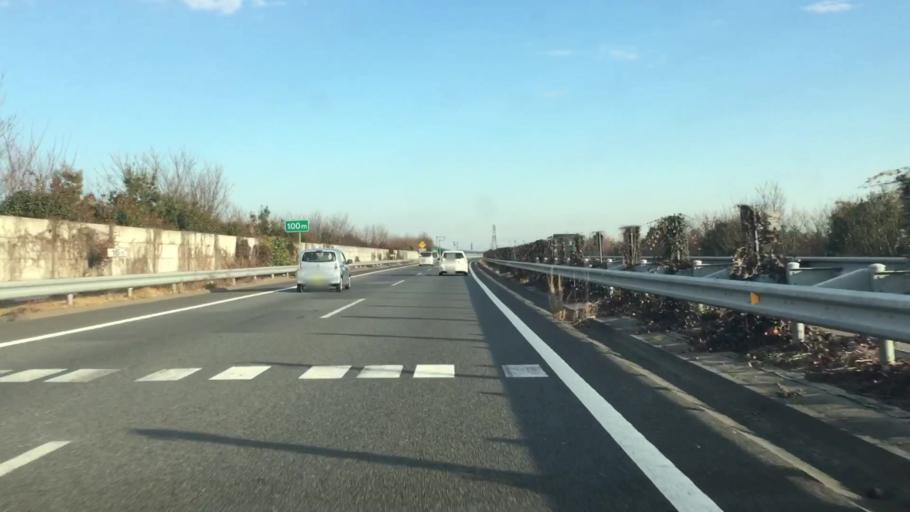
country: JP
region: Gunma
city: Isesaki
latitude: 36.3503
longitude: 139.2375
